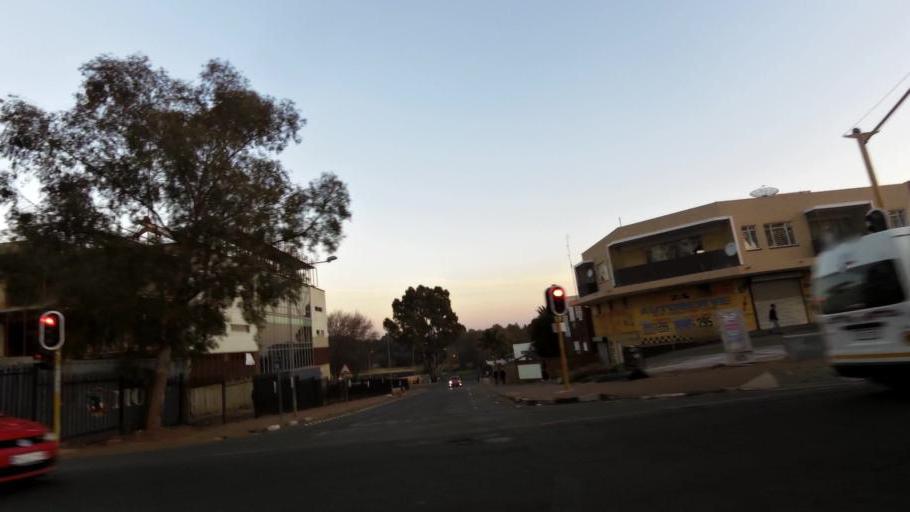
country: ZA
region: Gauteng
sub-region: City of Johannesburg Metropolitan Municipality
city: Johannesburg
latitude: -26.2019
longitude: 27.9974
